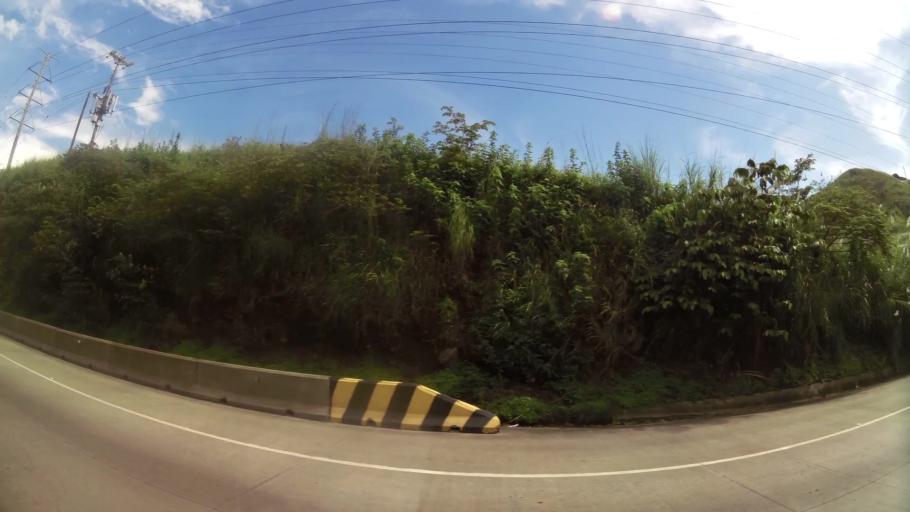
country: PA
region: Panama
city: Las Cumbres
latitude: 9.0551
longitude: -79.5167
